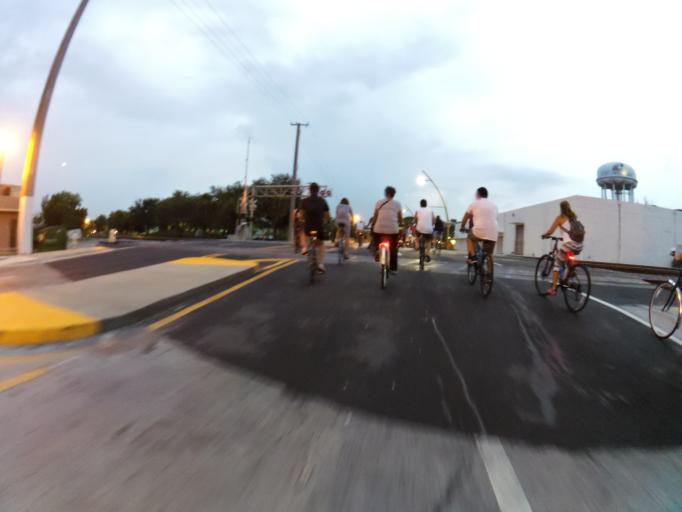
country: US
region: Florida
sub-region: Broward County
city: Fort Lauderdale
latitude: 26.1298
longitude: -80.1448
